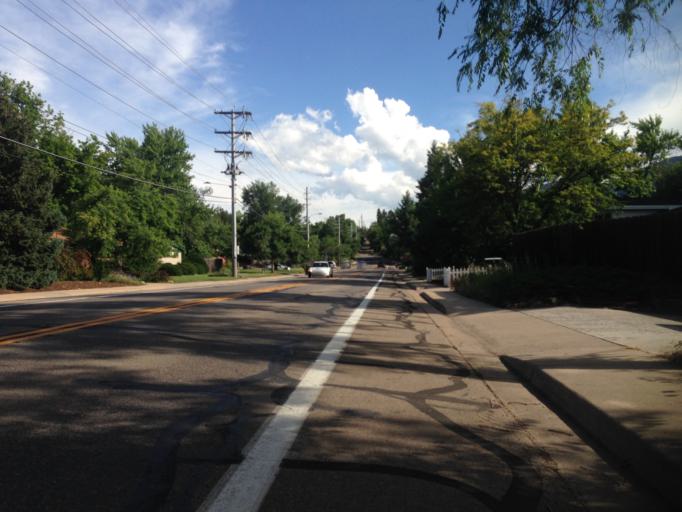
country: US
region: Colorado
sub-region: Boulder County
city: Boulder
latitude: 40.0278
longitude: -105.2727
